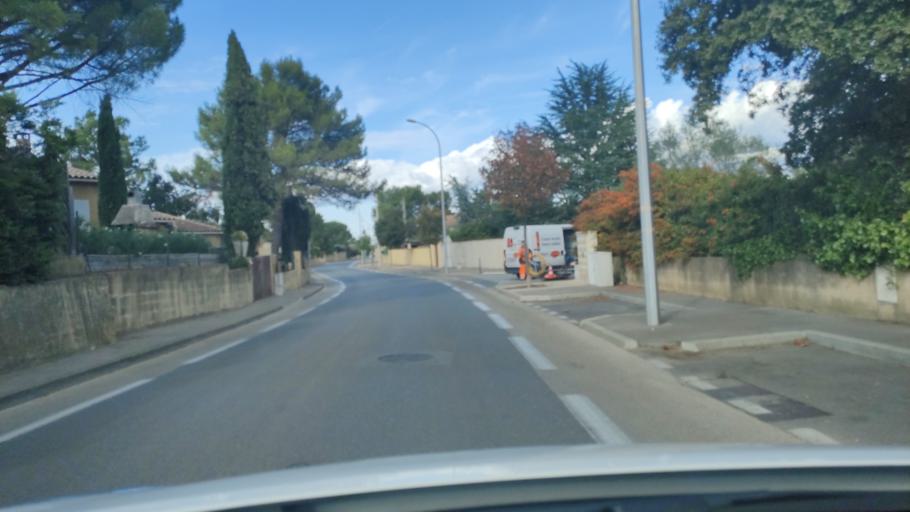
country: FR
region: Languedoc-Roussillon
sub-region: Departement du Gard
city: Villeneuve-les-Avignon
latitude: 43.9722
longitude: 4.7806
